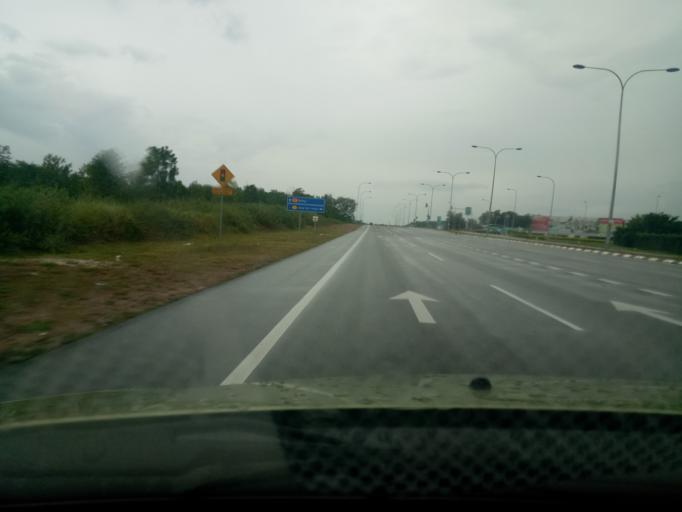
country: MY
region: Kedah
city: Sungai Petani
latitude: 5.6178
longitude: 100.5490
